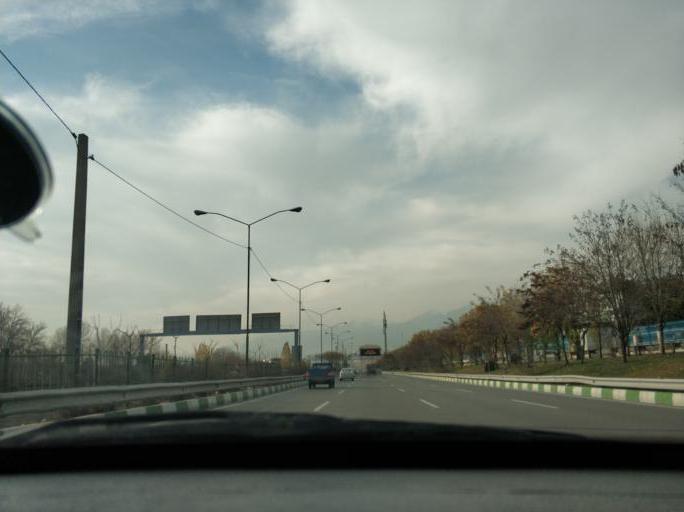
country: IR
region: Tehran
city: Tajrish
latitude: 35.7832
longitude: 51.5113
